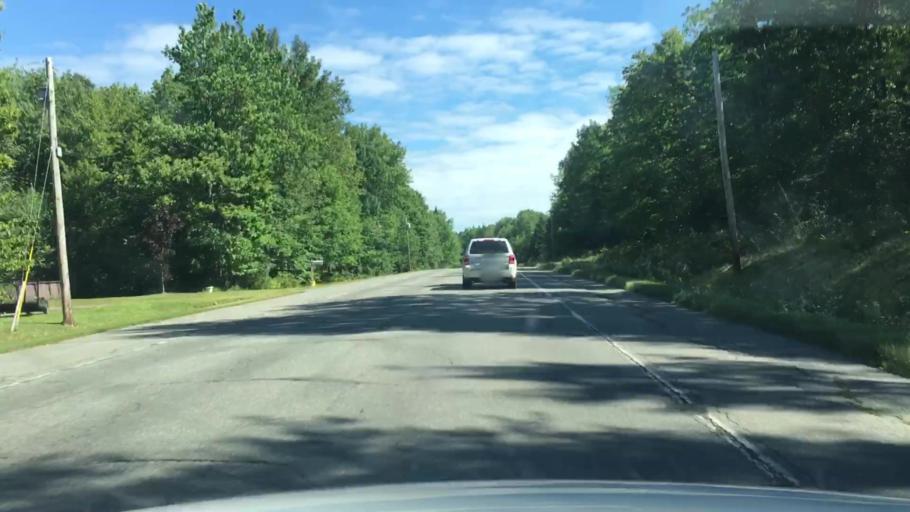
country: US
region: Maine
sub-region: Penobscot County
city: Dexter
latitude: 45.0497
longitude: -69.2653
